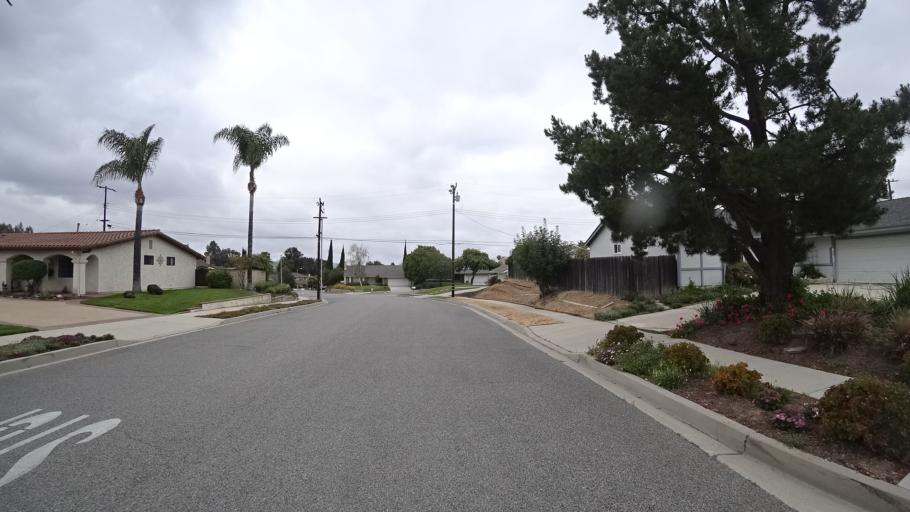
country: US
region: California
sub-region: Ventura County
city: Thousand Oaks
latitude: 34.2155
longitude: -118.8829
